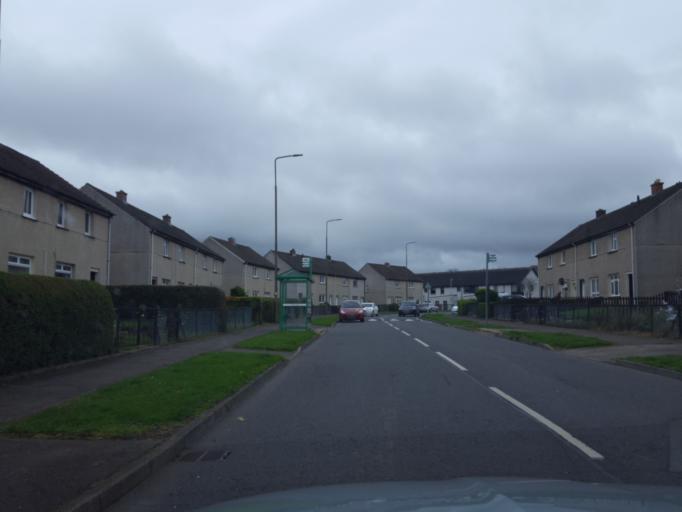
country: GB
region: Scotland
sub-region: Midlothian
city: Penicuik
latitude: 55.8323
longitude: -3.2109
